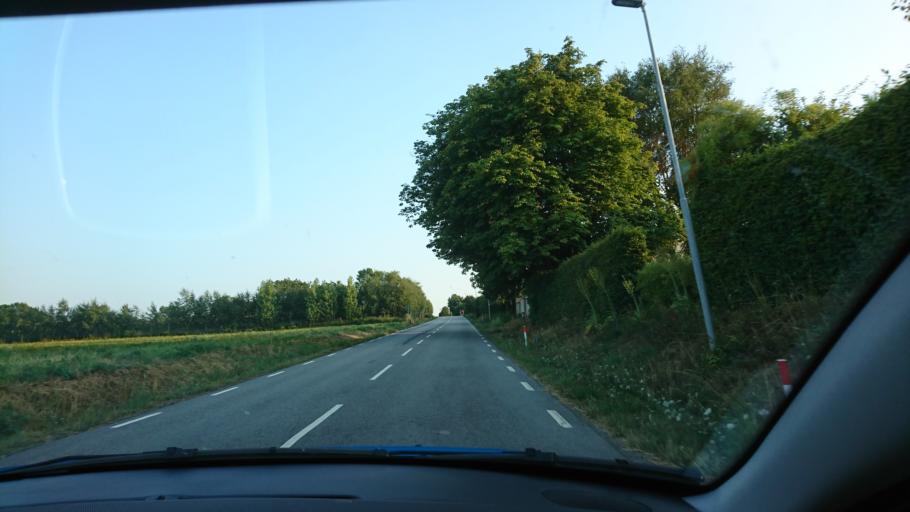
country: SE
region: Skane
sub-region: Simrishamns Kommun
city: Kivik
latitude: 55.7077
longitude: 14.1517
